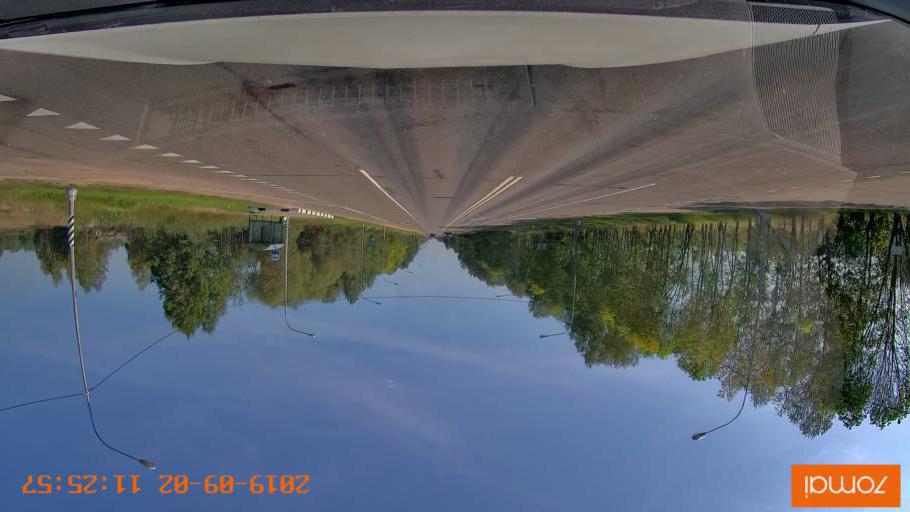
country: RU
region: Smolensk
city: Roslavl'
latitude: 53.9965
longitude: 32.9411
